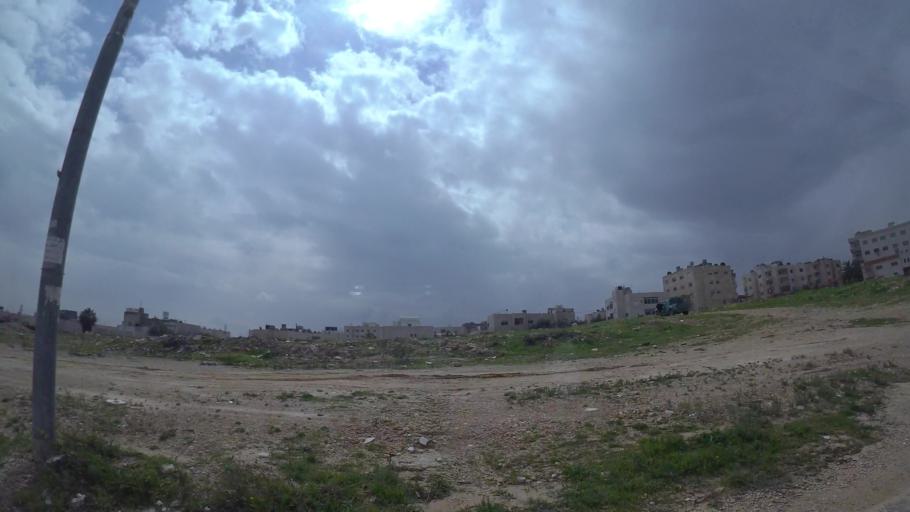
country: JO
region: Amman
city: Umm as Summaq
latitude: 31.9060
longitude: 35.8449
